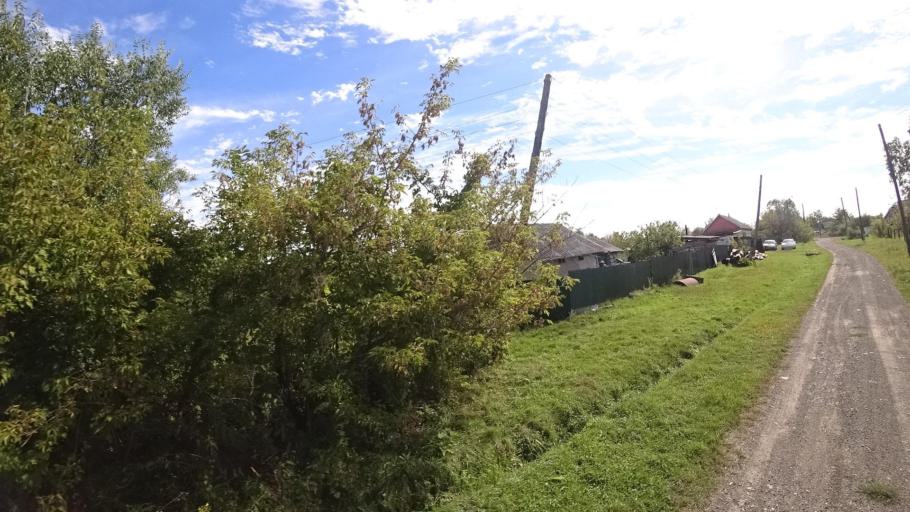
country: RU
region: Primorskiy
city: Yakovlevka
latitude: 44.4332
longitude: 133.5705
